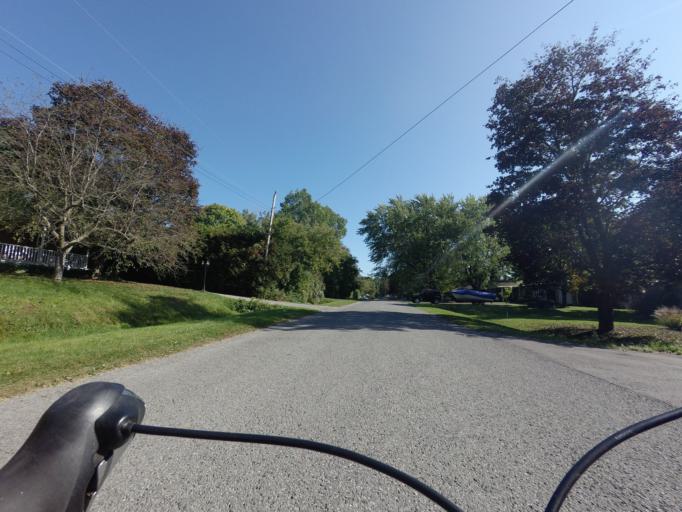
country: CA
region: Ontario
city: Bells Corners
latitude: 45.2309
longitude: -75.6881
